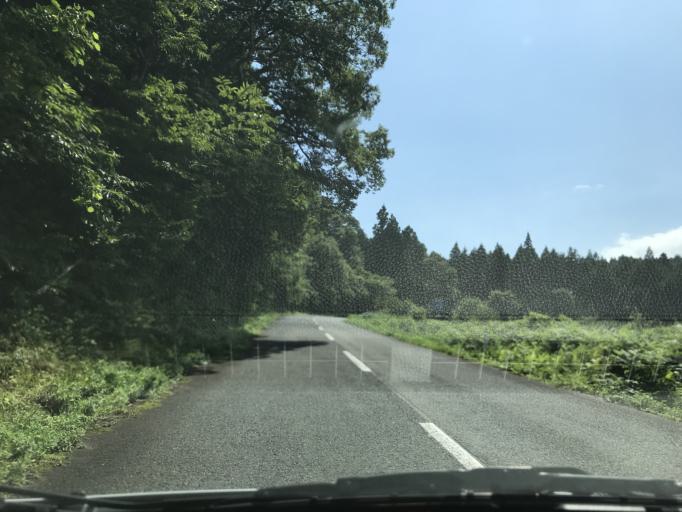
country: JP
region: Iwate
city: Ofunato
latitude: 38.9921
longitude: 141.4282
